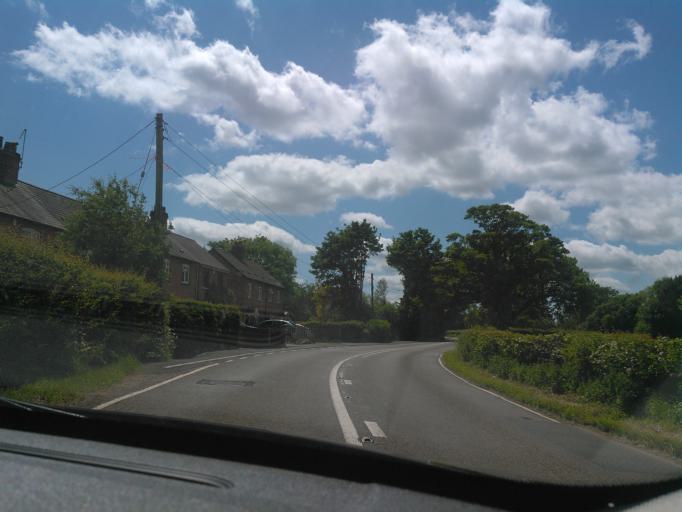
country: GB
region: England
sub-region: Shropshire
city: Prees
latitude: 52.8946
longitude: -2.6289
